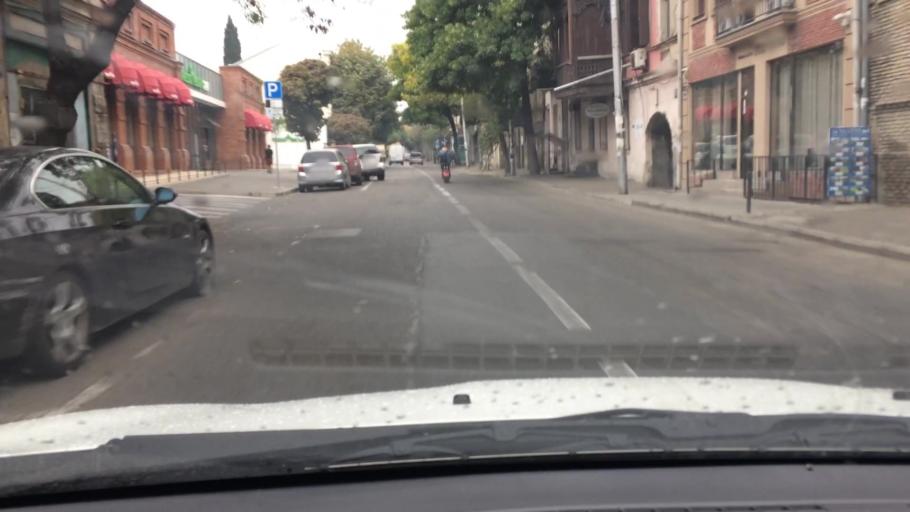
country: GE
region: T'bilisi
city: Tbilisi
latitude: 41.7072
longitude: 44.8053
